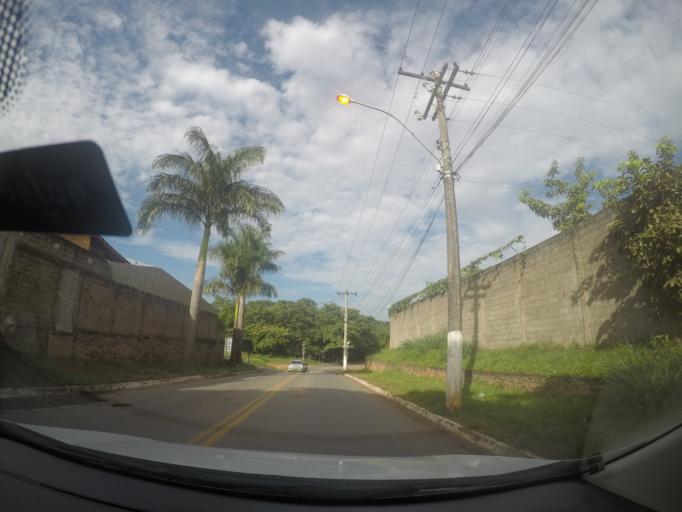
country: BR
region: Goias
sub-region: Goiania
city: Goiania
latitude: -16.6958
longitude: -49.1918
